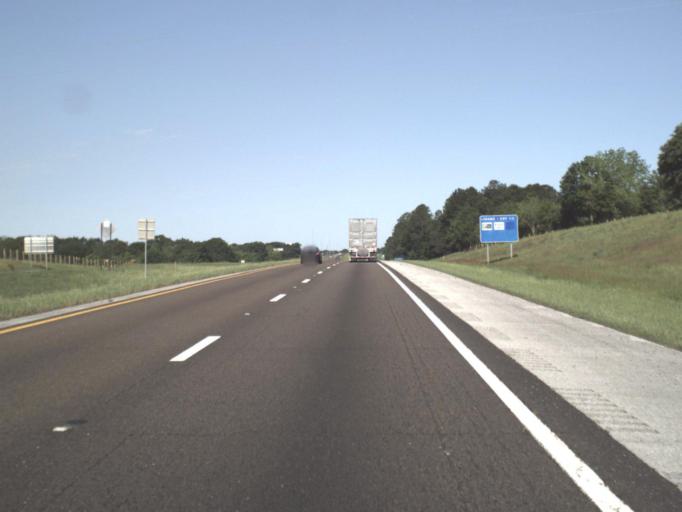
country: US
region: Florida
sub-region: Holmes County
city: Bonifay
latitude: 30.7624
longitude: -85.6680
